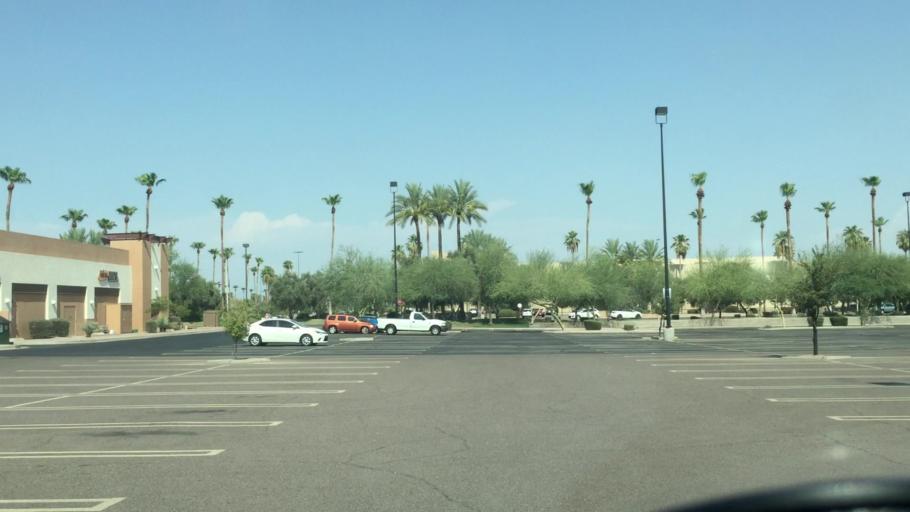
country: US
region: Arizona
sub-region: Maricopa County
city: Guadalupe
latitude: 33.3153
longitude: -111.9698
